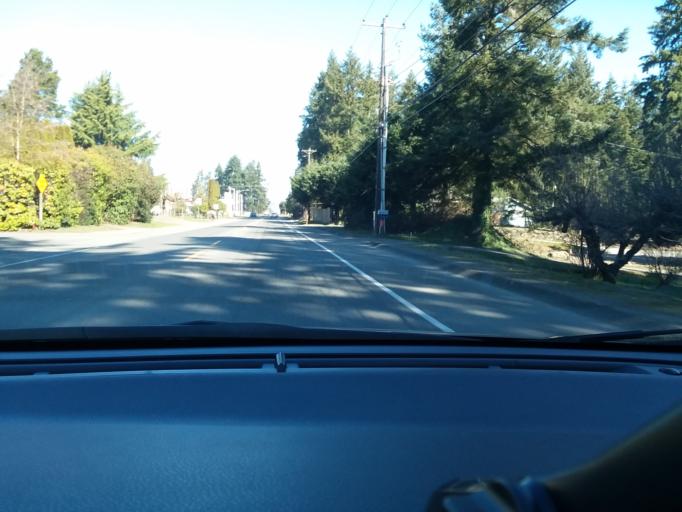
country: US
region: Washington
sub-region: Pierce County
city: Waller
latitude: 47.1893
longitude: -122.3573
